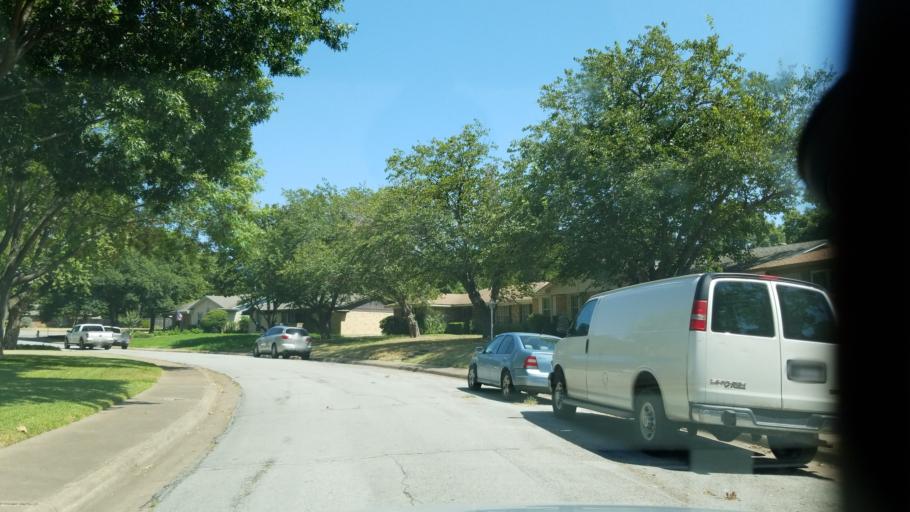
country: US
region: Texas
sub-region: Dallas County
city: Duncanville
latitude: 32.6522
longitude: -96.8983
